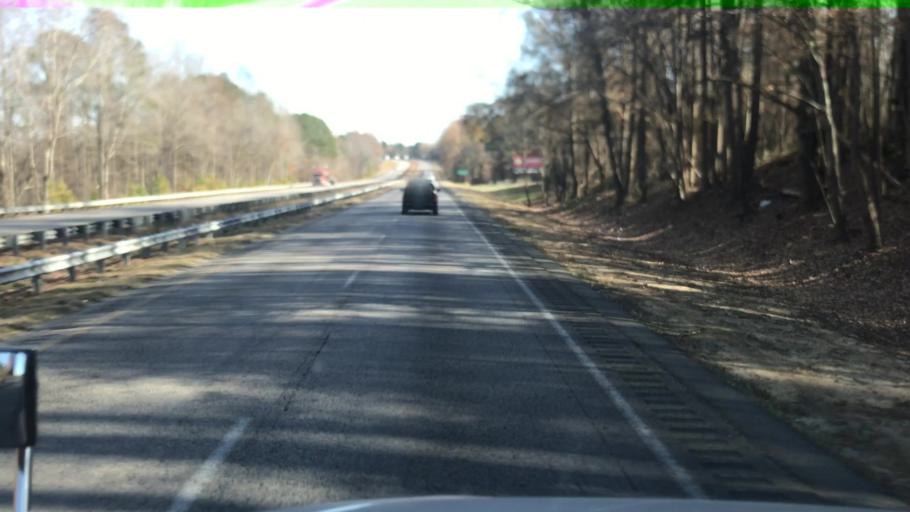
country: US
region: North Carolina
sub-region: Nash County
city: Nashville
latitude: 35.9768
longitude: -77.9234
